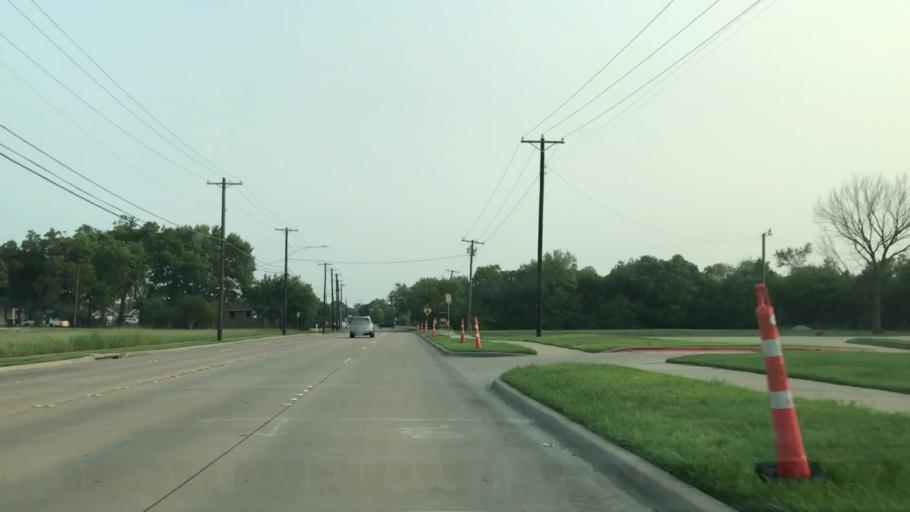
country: US
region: Texas
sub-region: Dallas County
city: Garland
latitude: 32.9039
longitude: -96.6219
